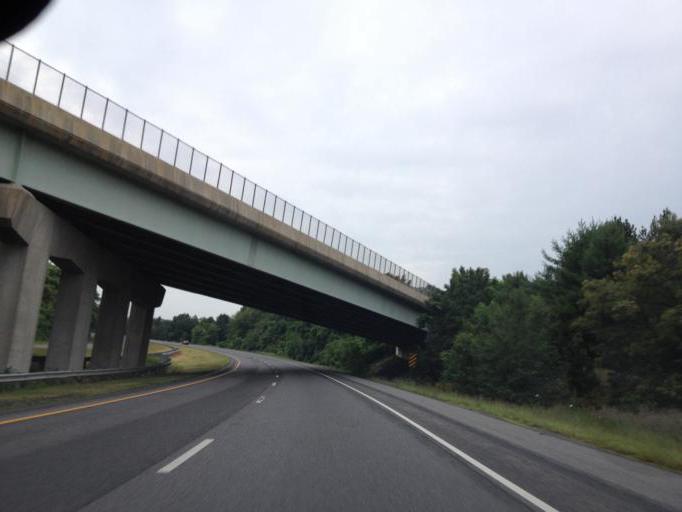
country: US
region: Maryland
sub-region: Anne Arundel County
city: Gambrills
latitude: 39.0675
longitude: -76.6403
